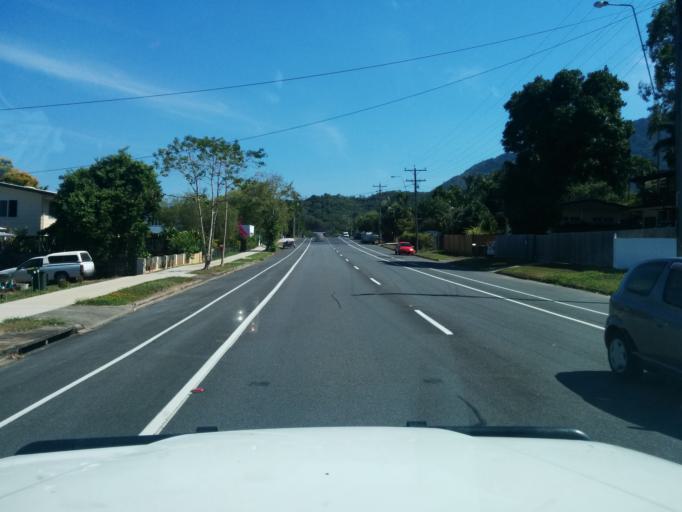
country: AU
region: Queensland
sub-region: Cairns
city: Redlynch
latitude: -16.9063
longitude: 145.7285
